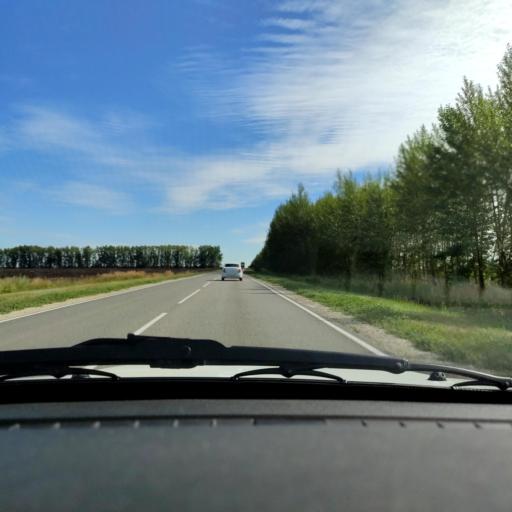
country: RU
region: Voronezj
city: Volya
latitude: 51.7231
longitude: 39.5468
